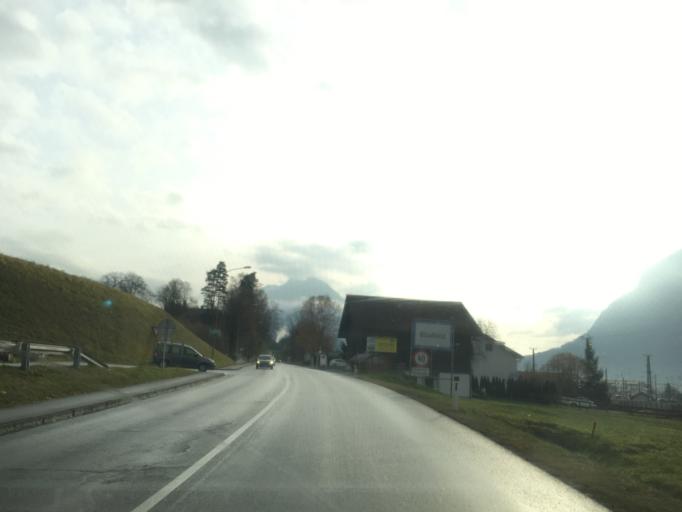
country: AT
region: Vorarlberg
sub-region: Politischer Bezirk Bludenz
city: Nuziders
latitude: 47.1601
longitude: 9.8071
